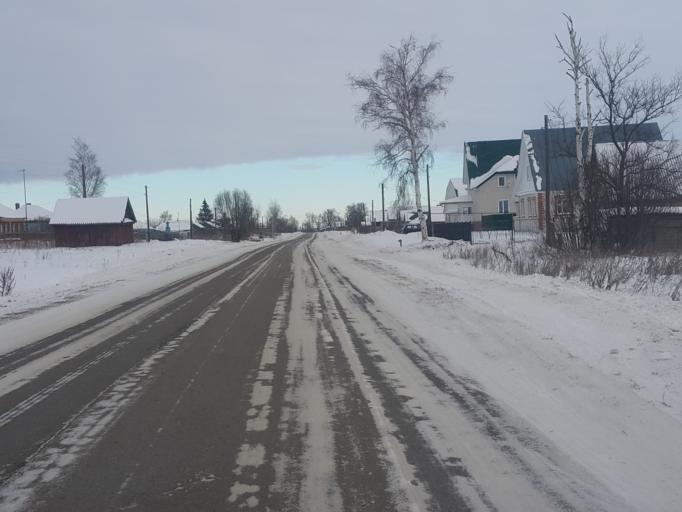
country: RU
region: Tambov
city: Platonovka
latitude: 52.8756
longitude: 41.8737
